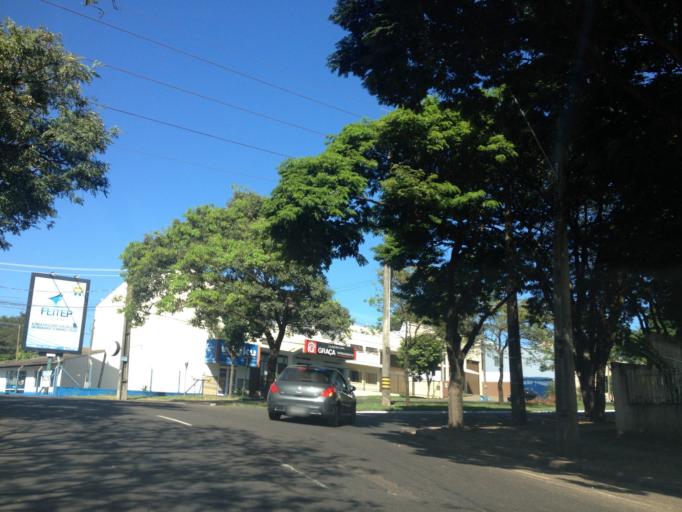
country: BR
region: Parana
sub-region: Maringa
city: Maringa
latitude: -23.4480
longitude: -51.9444
